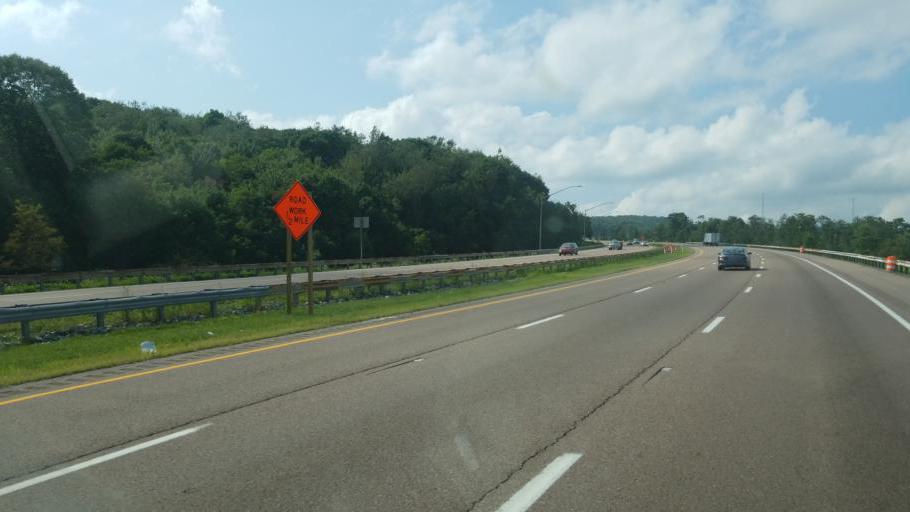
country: US
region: Maryland
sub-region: Allegany County
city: Frostburg
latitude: 39.6578
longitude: -78.9543
